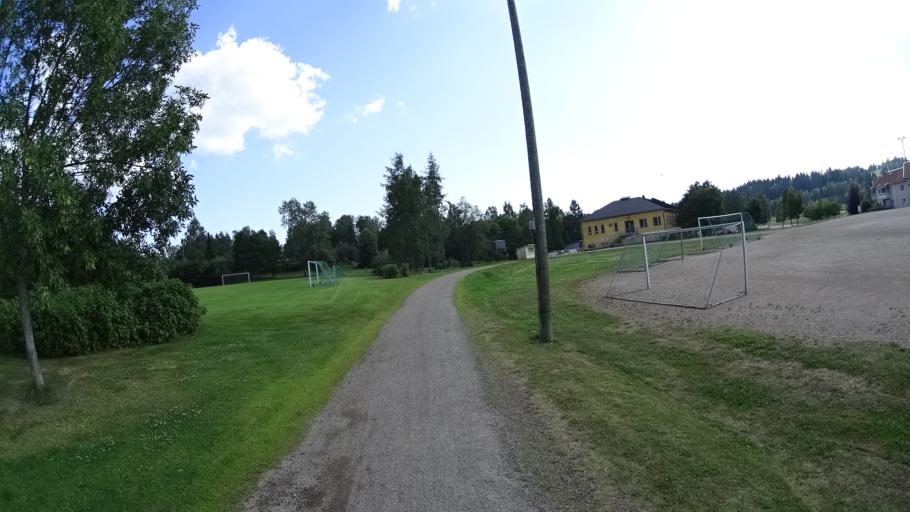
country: FI
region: Uusimaa
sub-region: Porvoo
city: Porvoo
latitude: 60.3867
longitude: 25.6712
